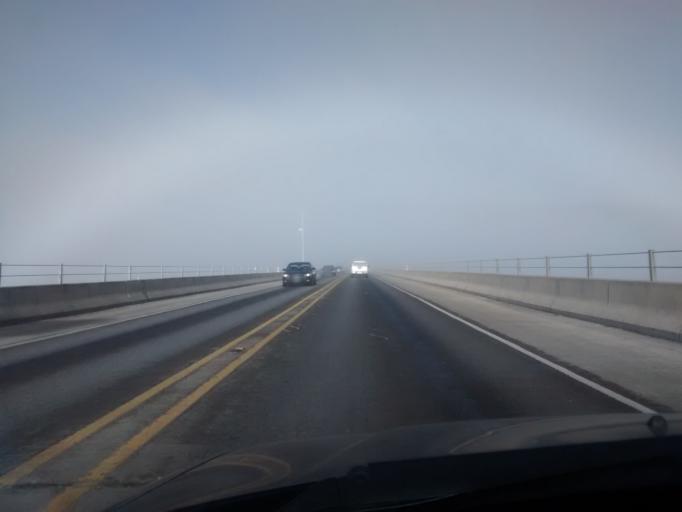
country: US
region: Washington
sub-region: Kitsap County
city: Lofall
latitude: 47.8628
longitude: -122.6296
